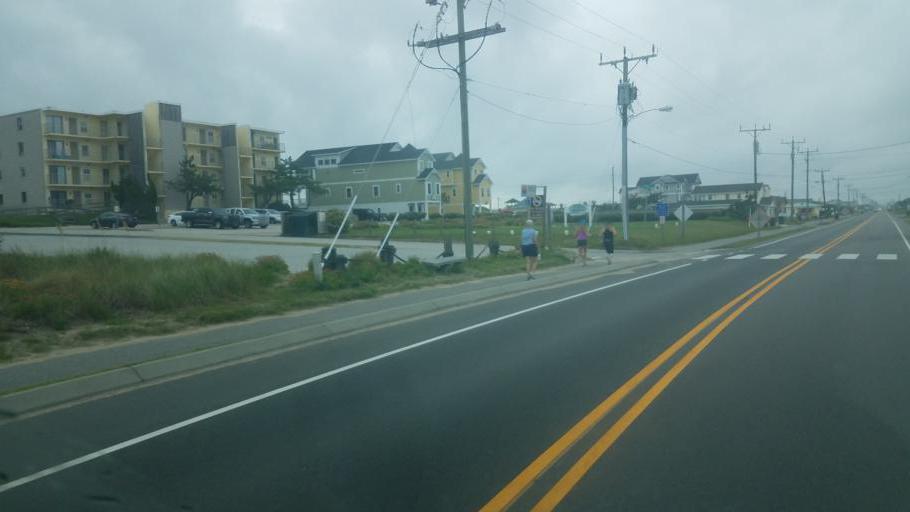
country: US
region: North Carolina
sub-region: Dare County
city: Nags Head
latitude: 35.9234
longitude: -75.6051
